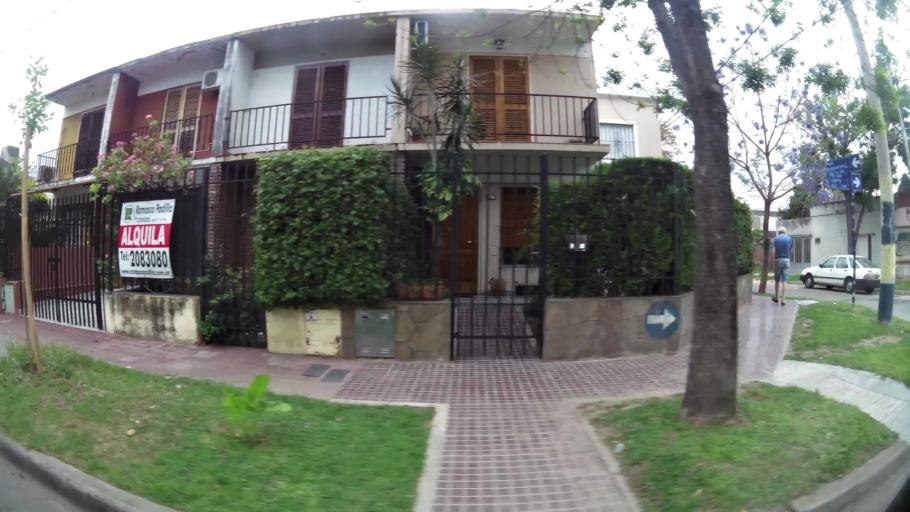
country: AR
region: Santa Fe
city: Granadero Baigorria
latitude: -32.8763
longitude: -60.6948
